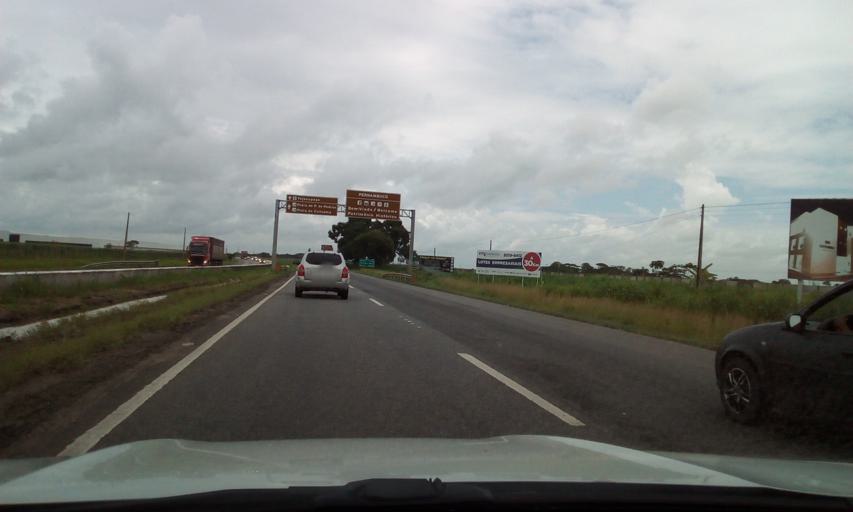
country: BR
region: Pernambuco
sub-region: Goiana
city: Goiana
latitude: -7.5051
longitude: -34.9864
